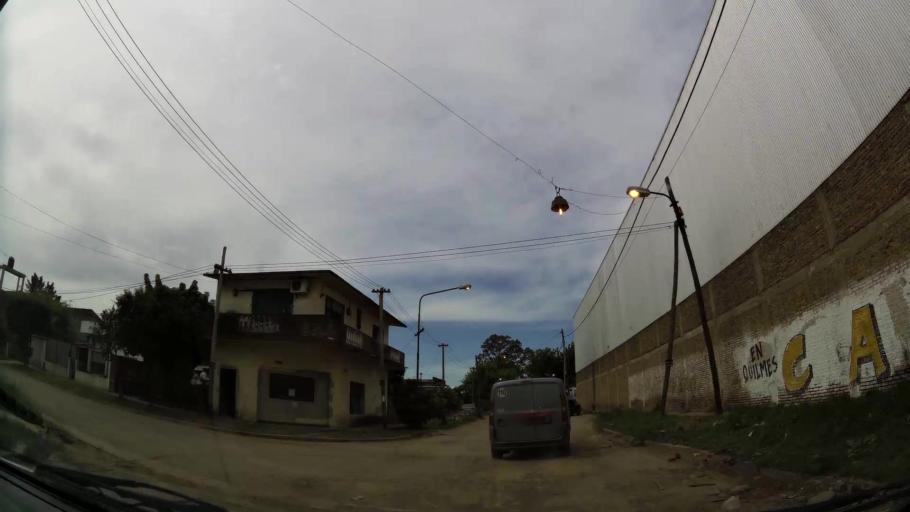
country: AR
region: Buenos Aires
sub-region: Partido de Quilmes
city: Quilmes
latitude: -34.7716
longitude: -58.2789
